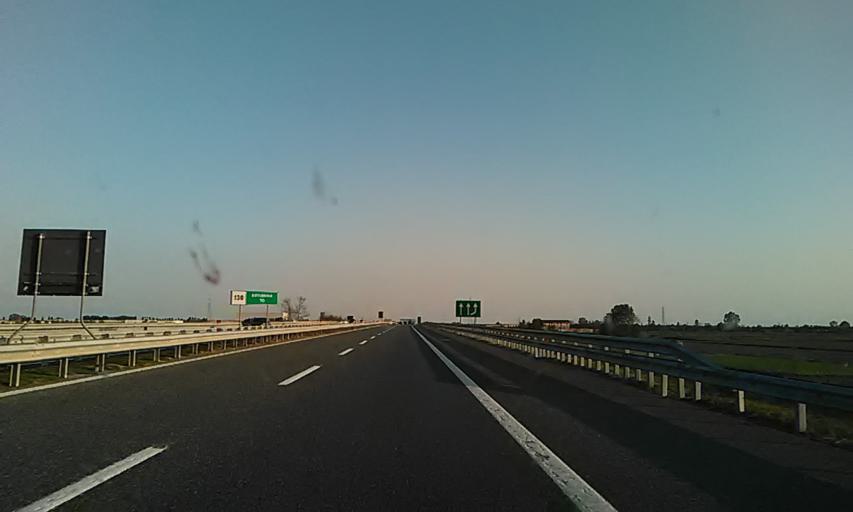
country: IT
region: Piedmont
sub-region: Provincia di Novara
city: Vicolungo
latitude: 45.4782
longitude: 8.4458
